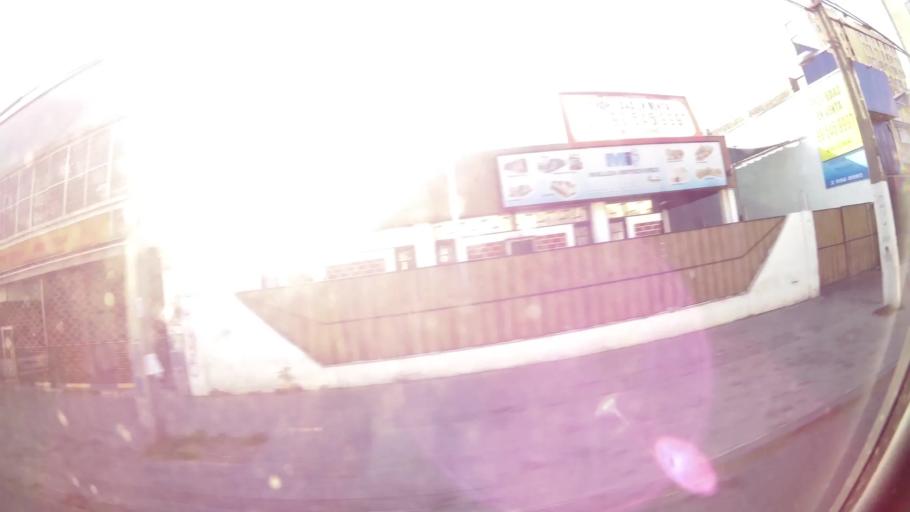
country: CL
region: Santiago Metropolitan
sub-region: Provincia de Santiago
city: Santiago
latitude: -33.4640
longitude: -70.6471
